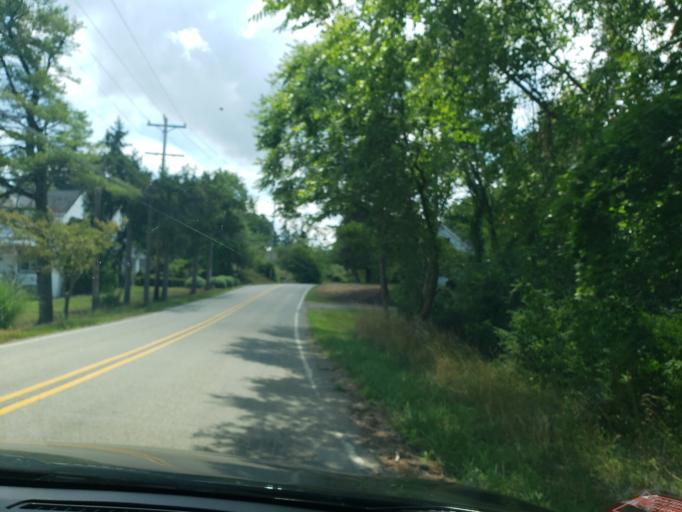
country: US
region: Pennsylvania
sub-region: Allegheny County
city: Coraopolis
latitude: 40.5387
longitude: -80.1414
